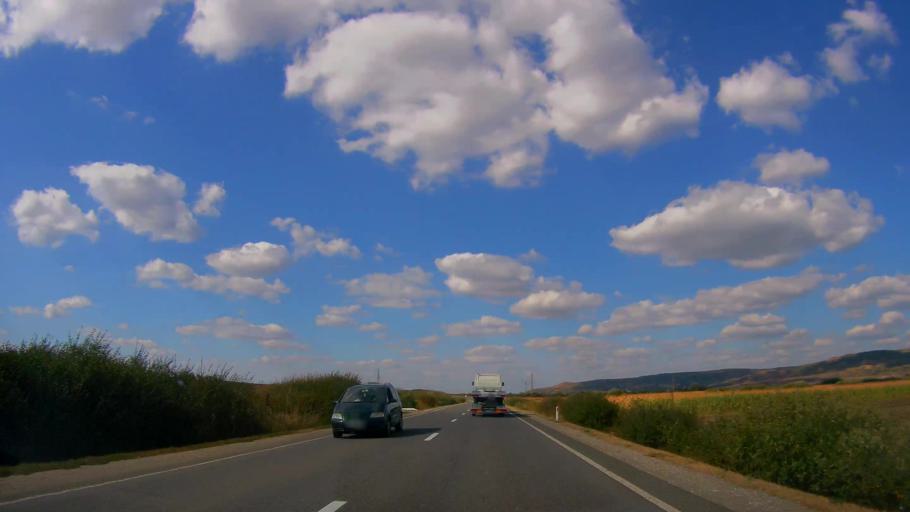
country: RO
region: Salaj
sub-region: Comuna Sarmasag
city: Sarmasag
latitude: 47.3537
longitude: 22.7995
